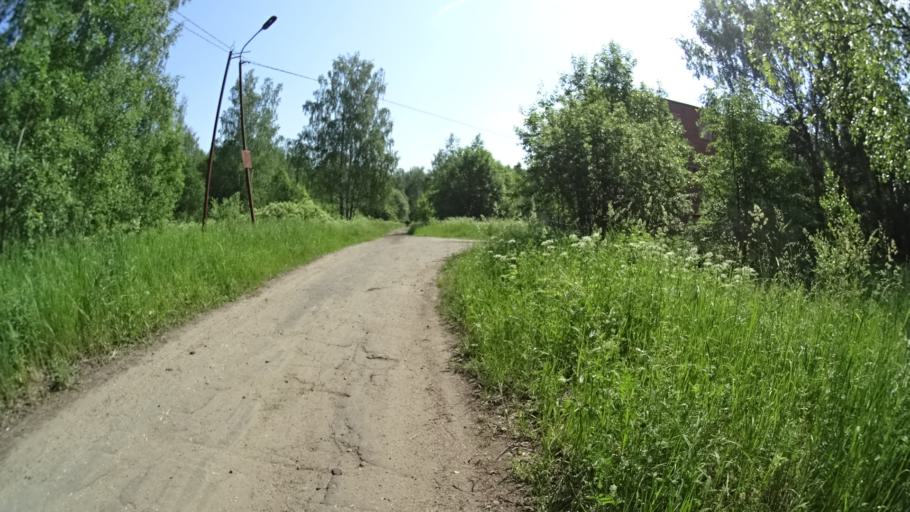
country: RU
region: Moskovskaya
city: Lesnoy
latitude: 56.0800
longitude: 37.9438
